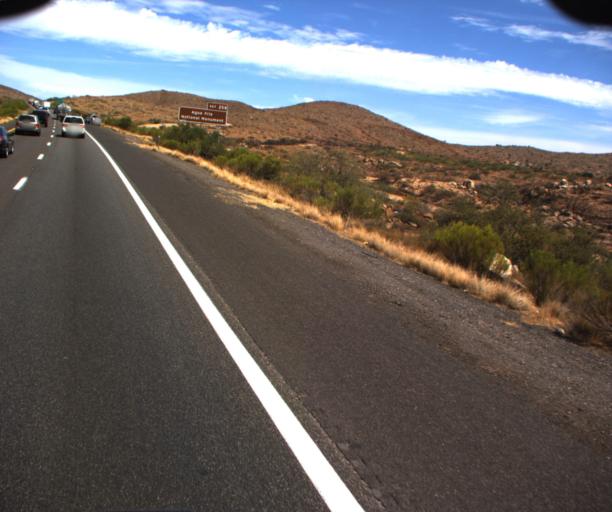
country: US
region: Arizona
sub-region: Yavapai County
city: Cordes Lakes
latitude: 34.2759
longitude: -112.1145
